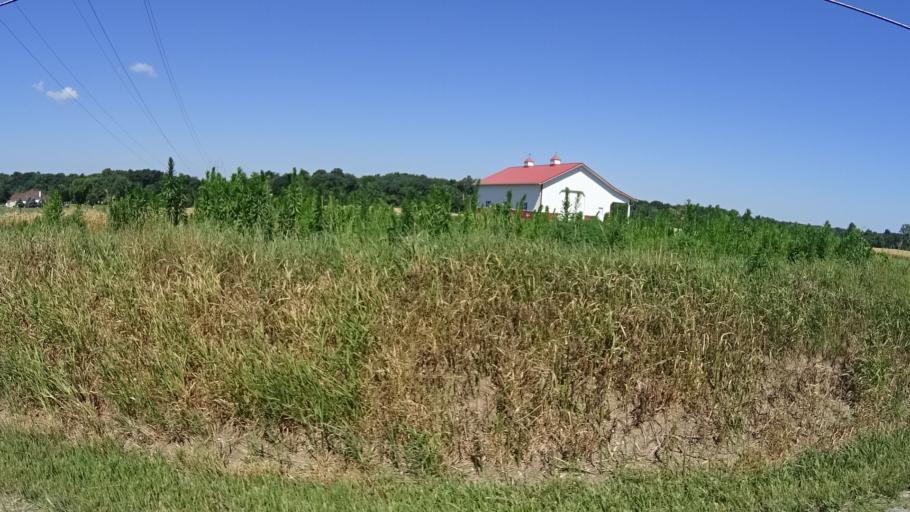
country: US
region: Ohio
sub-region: Erie County
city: Huron
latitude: 41.3598
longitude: -82.5745
